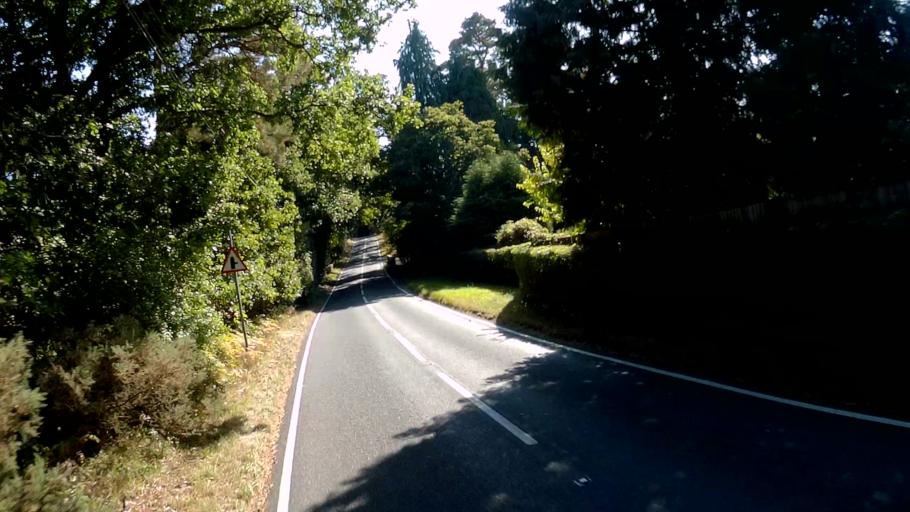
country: GB
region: England
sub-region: Surrey
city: Farnham
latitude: 51.1981
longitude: -0.7730
